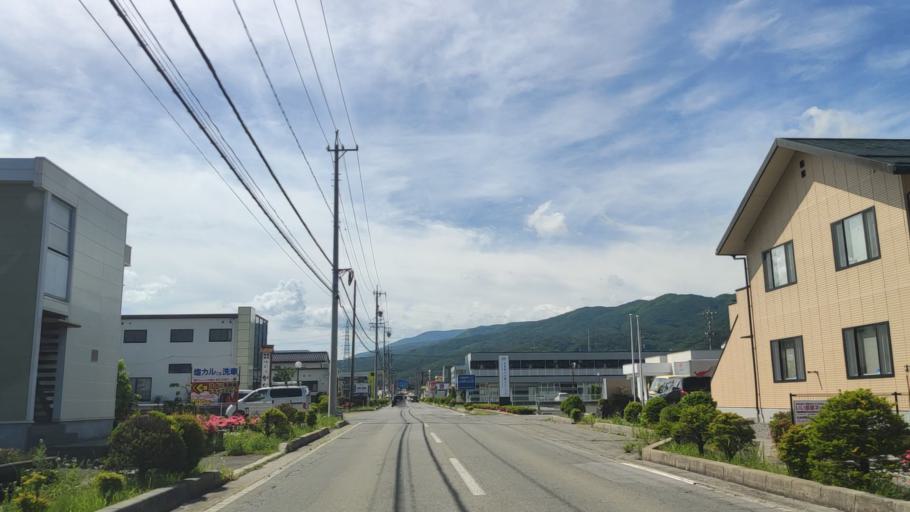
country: JP
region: Nagano
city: Chino
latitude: 36.0008
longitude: 138.1417
